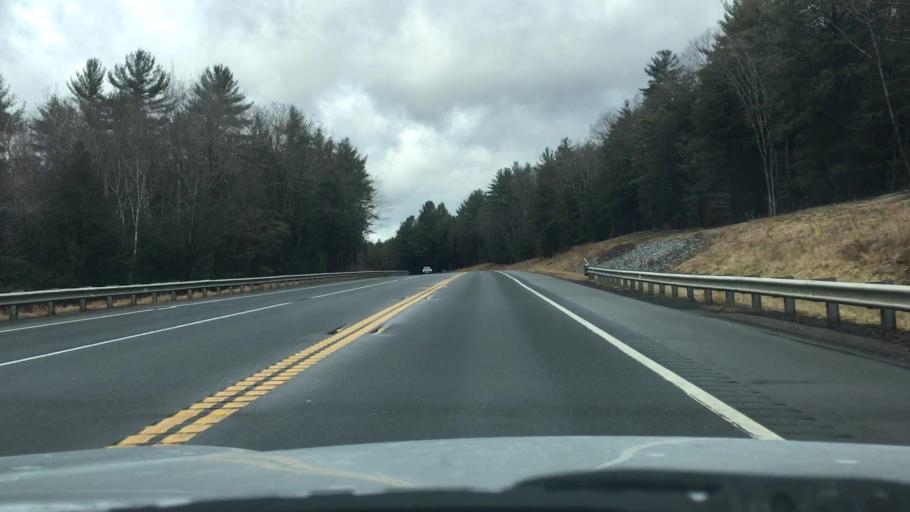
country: US
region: Massachusetts
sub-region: Franklin County
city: Orange
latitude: 42.5826
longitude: -72.3256
